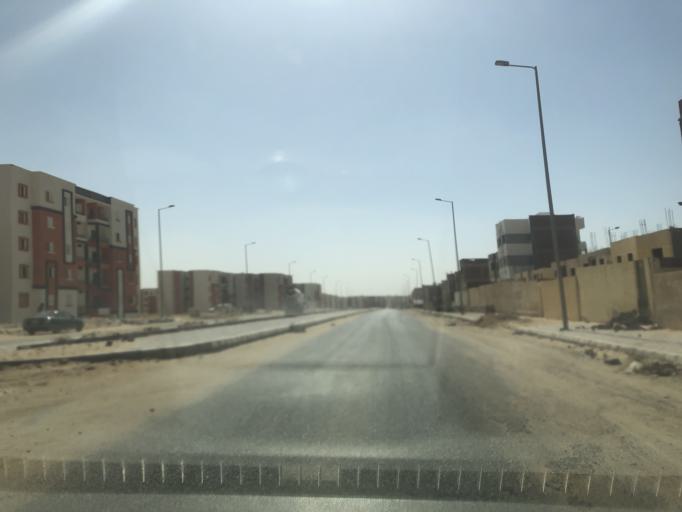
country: EG
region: Al Jizah
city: Madinat Sittah Uktubar
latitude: 29.9276
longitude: 31.0015
